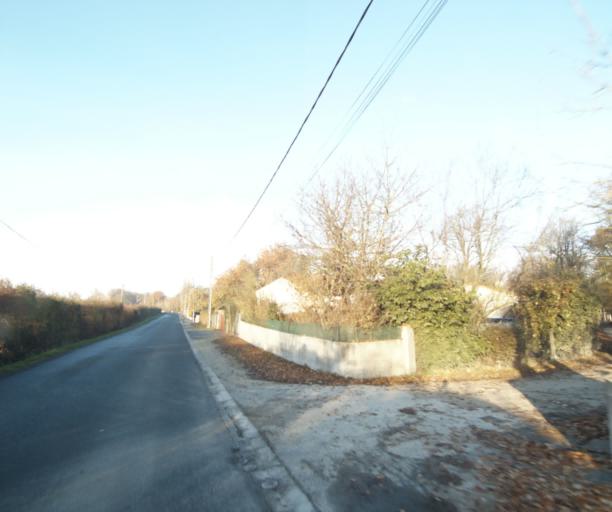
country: FR
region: Poitou-Charentes
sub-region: Departement de la Charente-Maritime
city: Fontcouverte
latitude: 45.7633
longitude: -0.5946
